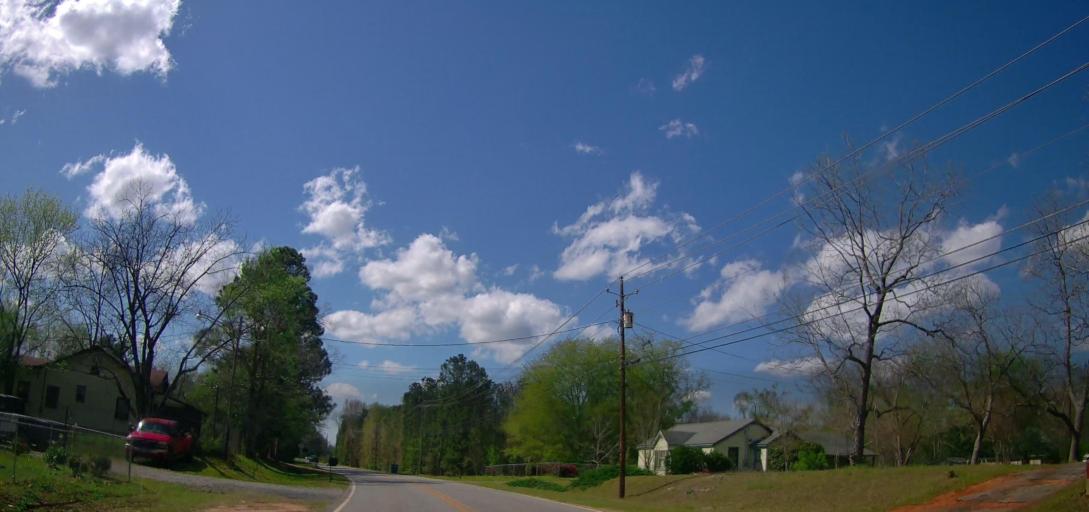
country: US
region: Georgia
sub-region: Bibb County
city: Macon
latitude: 32.8339
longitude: -83.5634
